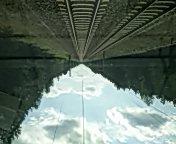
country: DE
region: Brandenburg
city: Halbe
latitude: 52.1225
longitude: 13.6868
